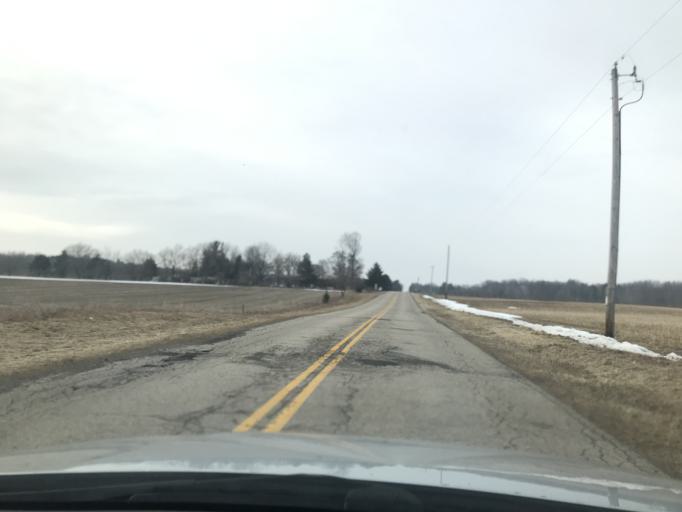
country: US
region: Wisconsin
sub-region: Oconto County
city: Oconto Falls
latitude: 44.8311
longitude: -88.1683
